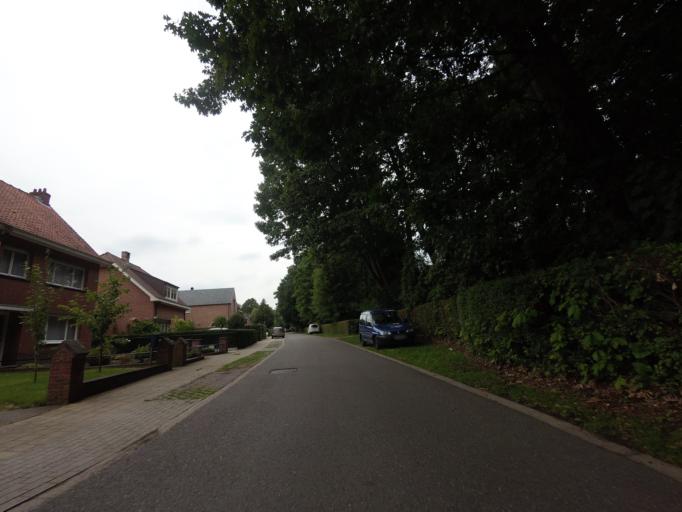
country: BE
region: Flanders
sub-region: Provincie Antwerpen
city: Schilde
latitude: 51.2339
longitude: 4.5862
